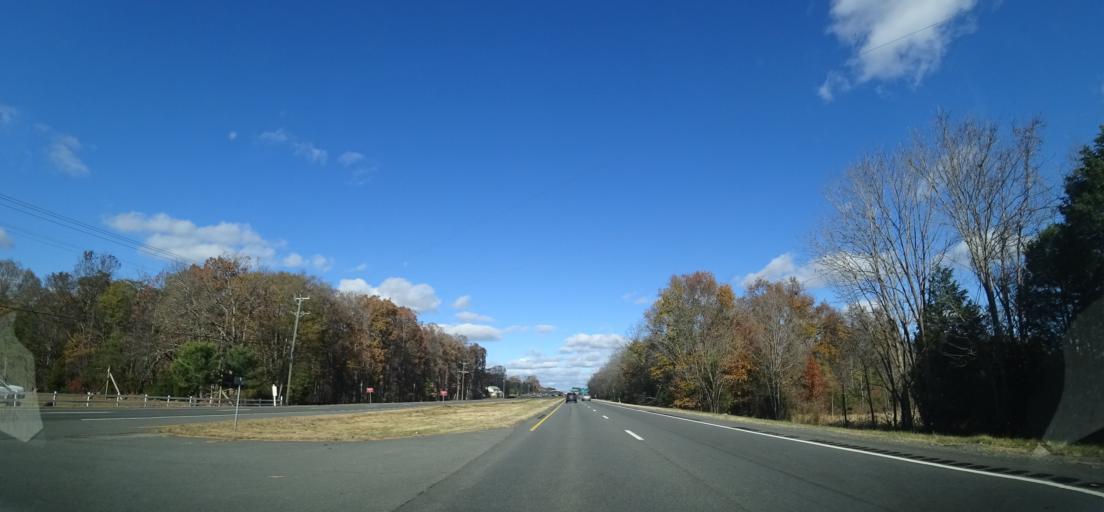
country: US
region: Virginia
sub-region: Fauquier County
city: Bealeton
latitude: 38.6041
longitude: -77.8003
